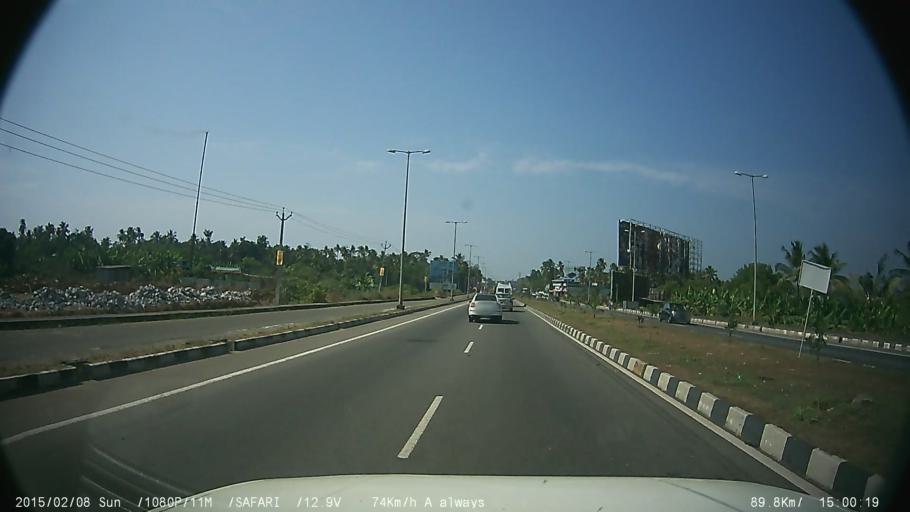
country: IN
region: Kerala
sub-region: Thrissur District
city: Kizhake Chalakudi
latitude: 10.3157
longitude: 76.3285
